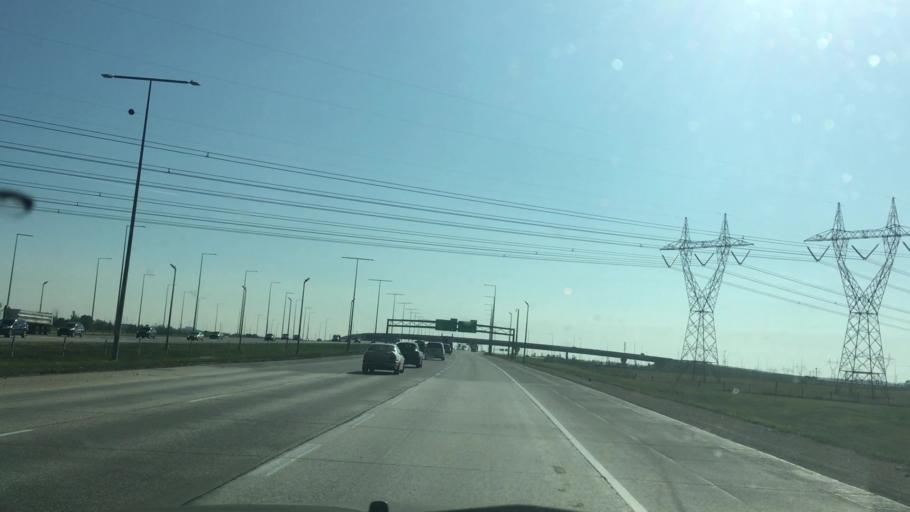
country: CA
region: Alberta
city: Edmonton
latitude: 53.4348
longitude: -113.5066
